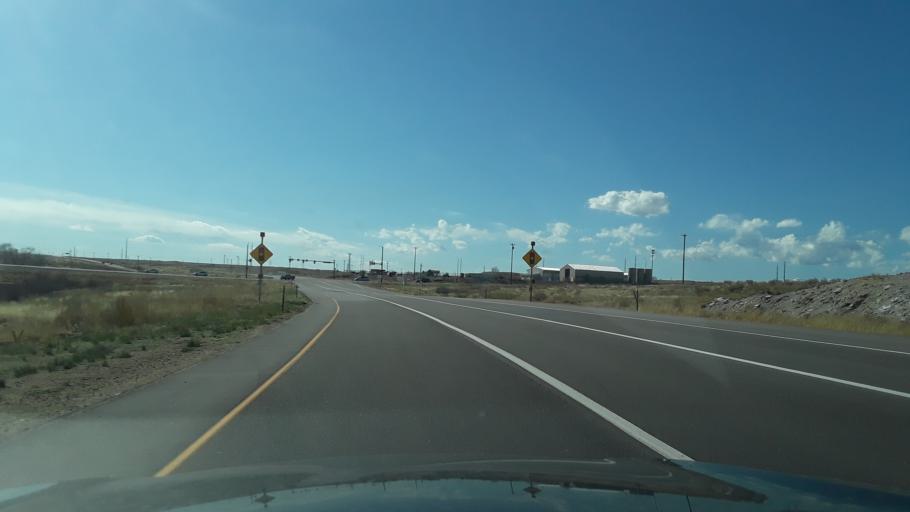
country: US
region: Colorado
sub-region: Pueblo County
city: Pueblo West
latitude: 38.3146
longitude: -104.6577
